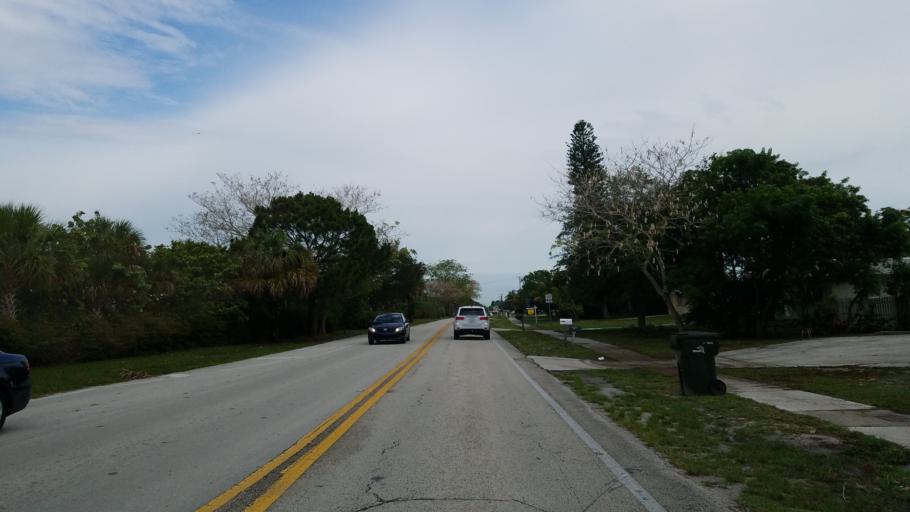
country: US
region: Florida
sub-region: Martin County
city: Stuart
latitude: 27.1829
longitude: -80.2378
